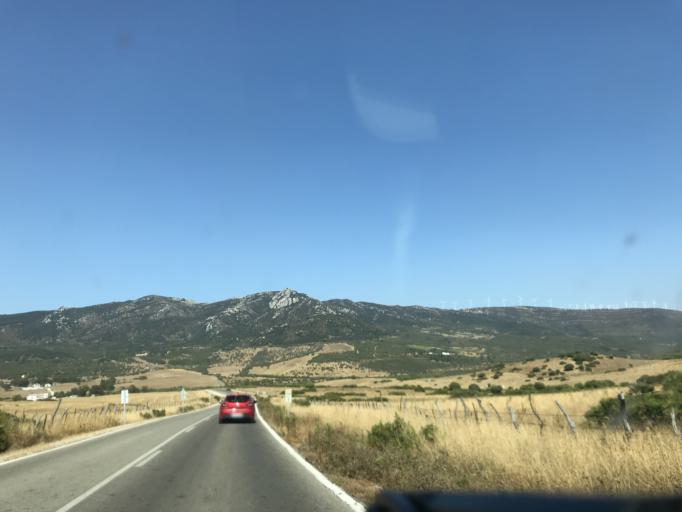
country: ES
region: Andalusia
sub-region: Provincia de Cadiz
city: Zahara de los Atunes
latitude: 36.1041
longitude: -5.7197
